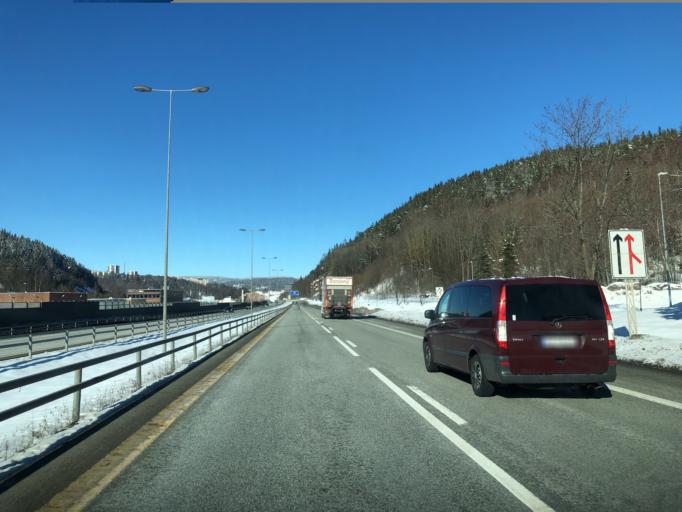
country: NO
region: Buskerud
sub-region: Drammen
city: Skoger
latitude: 59.7024
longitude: 10.2440
